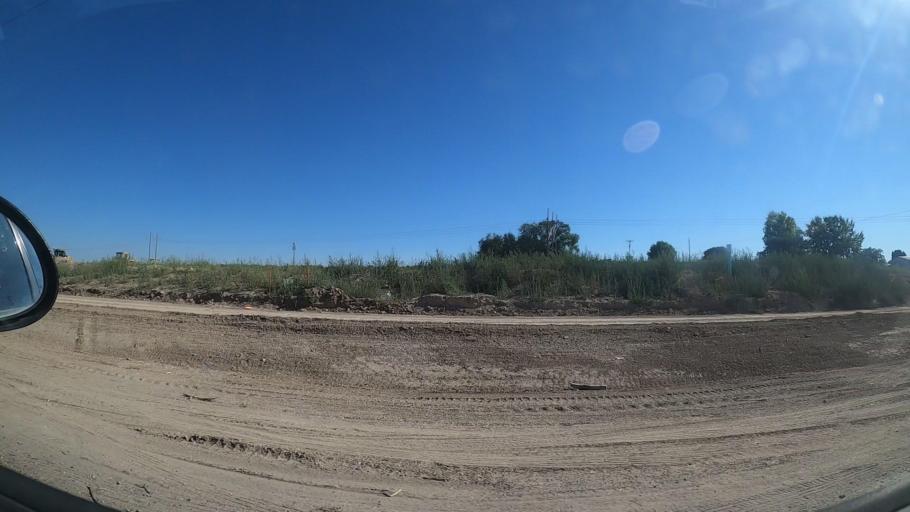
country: US
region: Idaho
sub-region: Canyon County
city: Nampa
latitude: 43.5476
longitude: -116.6126
